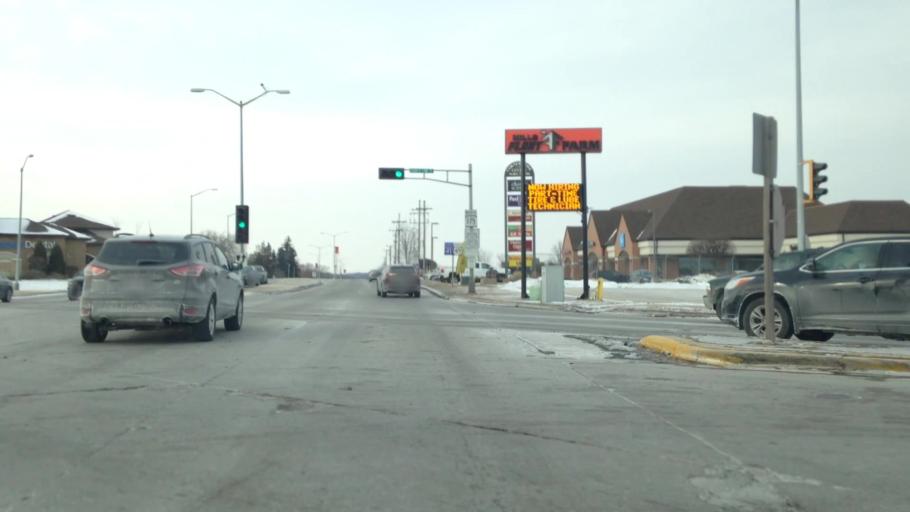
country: US
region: Wisconsin
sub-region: Waukesha County
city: Menomonee Falls
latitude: 43.1919
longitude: -88.1361
